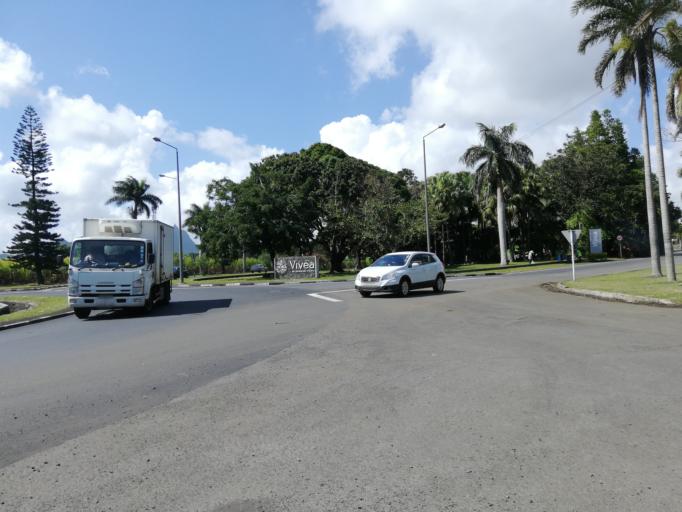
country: MU
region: Moka
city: Saint Pierre
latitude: -20.2240
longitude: 57.5306
